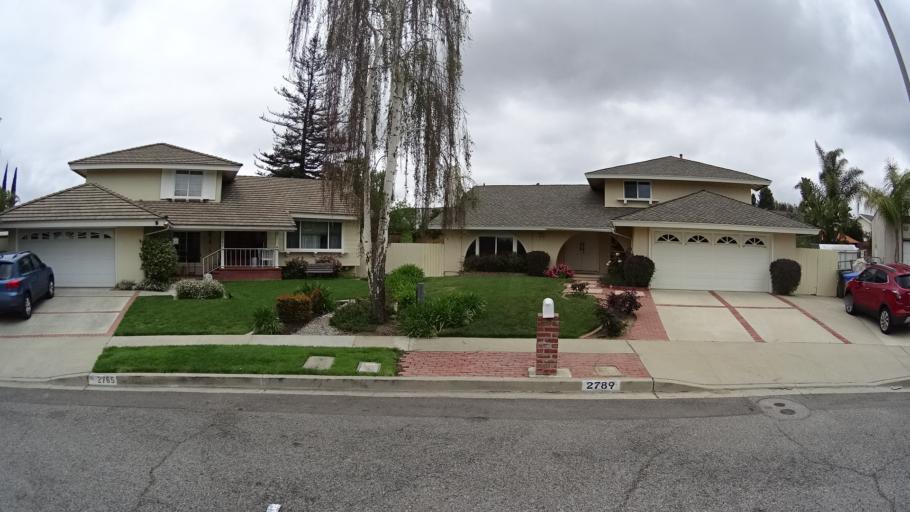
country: US
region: California
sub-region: Ventura County
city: Thousand Oaks
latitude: 34.2158
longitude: -118.8845
